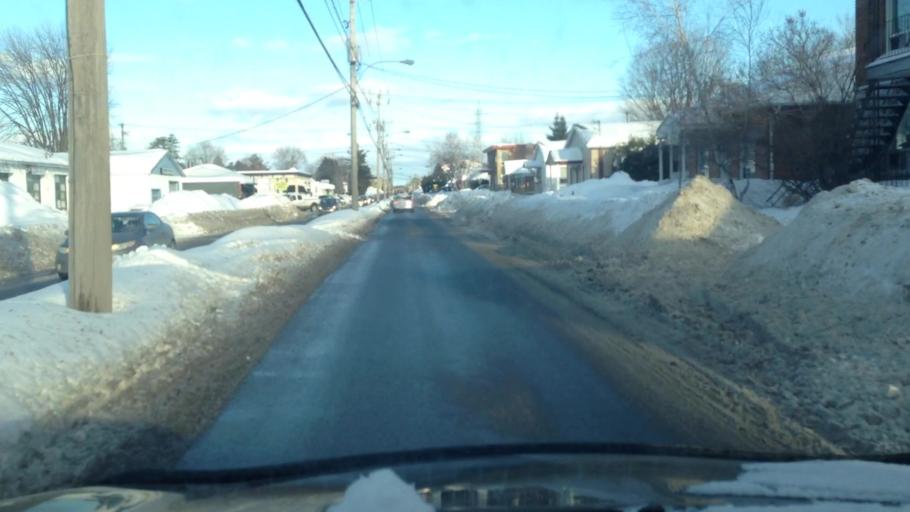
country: CA
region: Quebec
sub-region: Laurentides
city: Saint-Jerome
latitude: 45.7946
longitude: -74.0049
